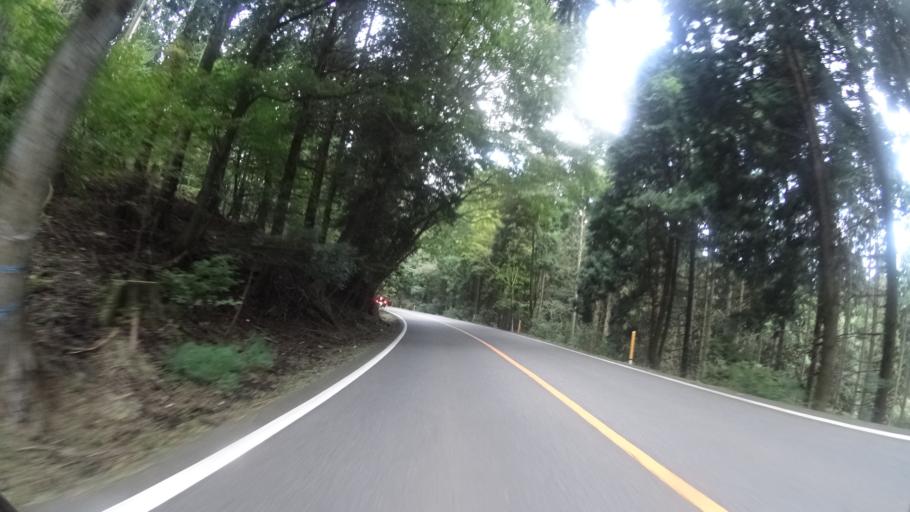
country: JP
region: Oita
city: Beppu
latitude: 33.2730
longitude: 131.4111
